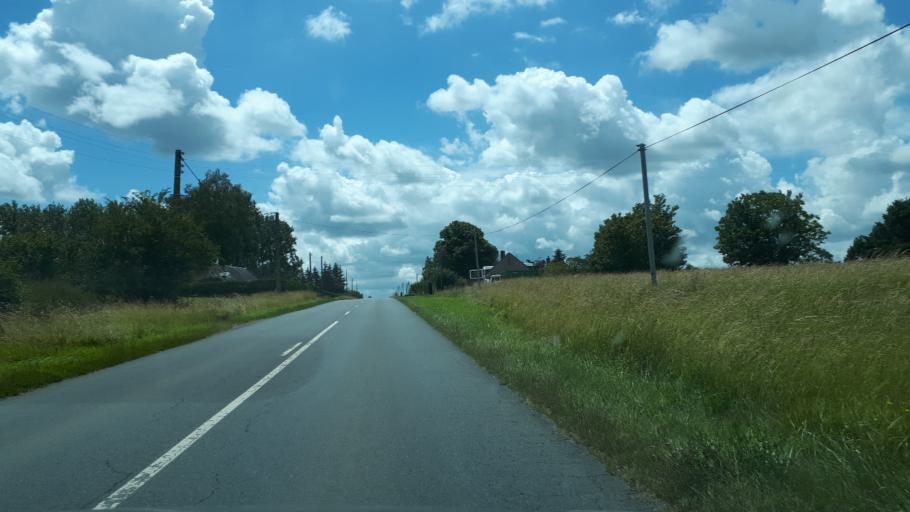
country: FR
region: Centre
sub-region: Departement du Loir-et-Cher
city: Contres
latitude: 47.4055
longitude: 1.4185
